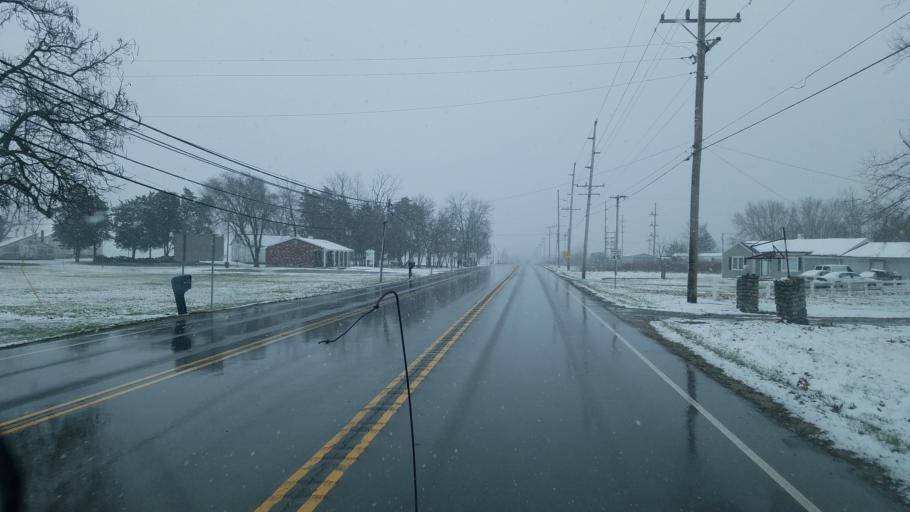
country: US
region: Indiana
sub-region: Wayne County
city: Richmond
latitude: 39.8781
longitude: -84.9409
